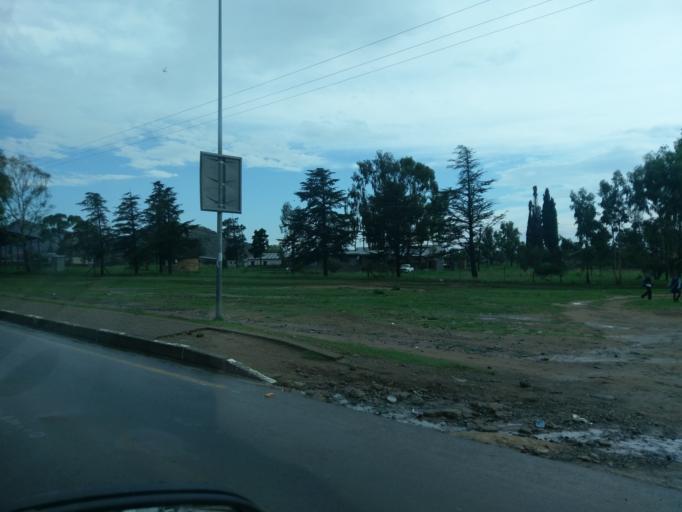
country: LS
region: Mafeteng
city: Mafeteng
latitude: -29.8185
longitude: 27.2364
